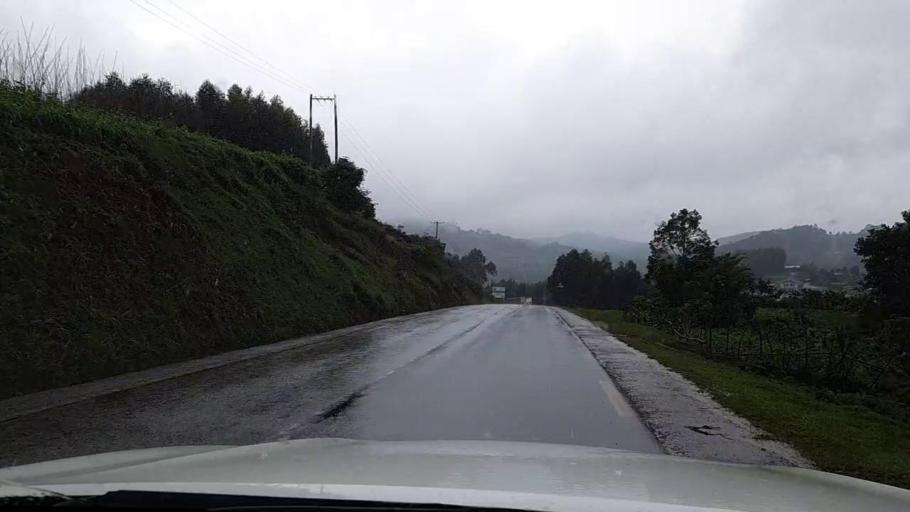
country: RW
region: Western Province
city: Cyangugu
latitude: -2.4633
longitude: 28.9868
